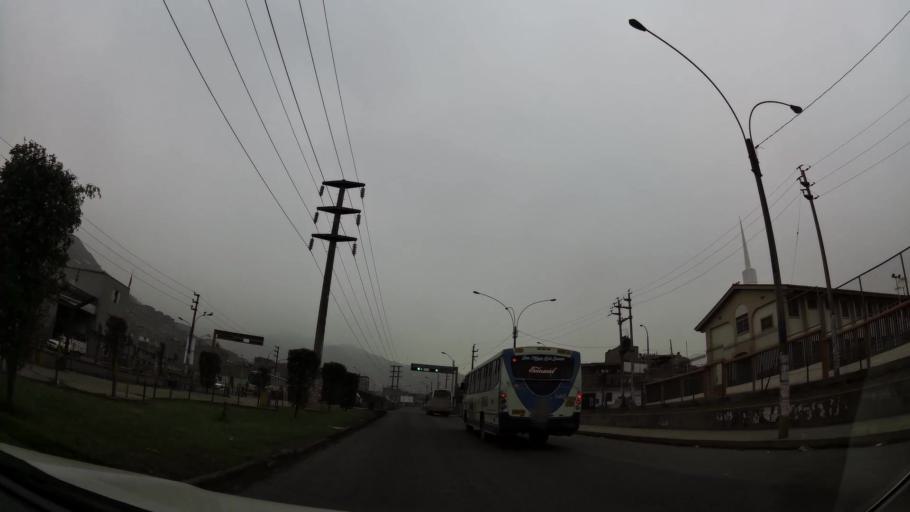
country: PE
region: Lima
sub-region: Lima
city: Independencia
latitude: -11.9413
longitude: -76.9806
